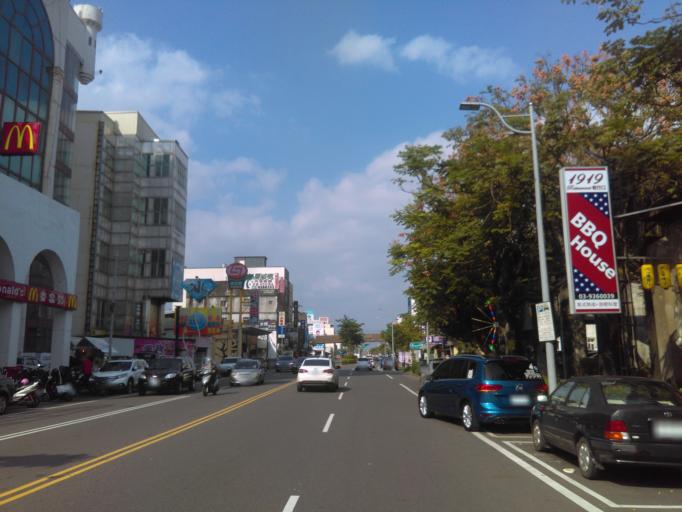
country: TW
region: Taiwan
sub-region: Yilan
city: Yilan
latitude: 24.7563
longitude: 121.7581
